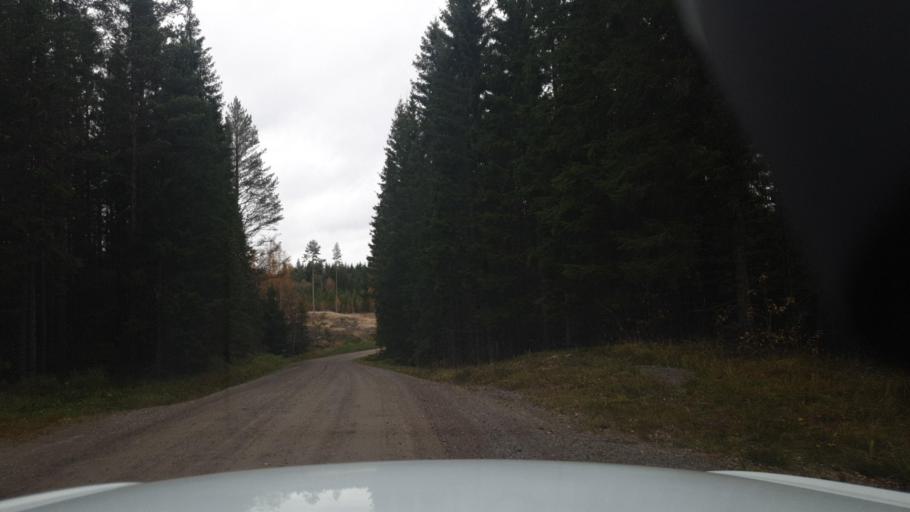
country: SE
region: Vaermland
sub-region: Arvika Kommun
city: Arvika
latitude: 59.9577
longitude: 12.6596
